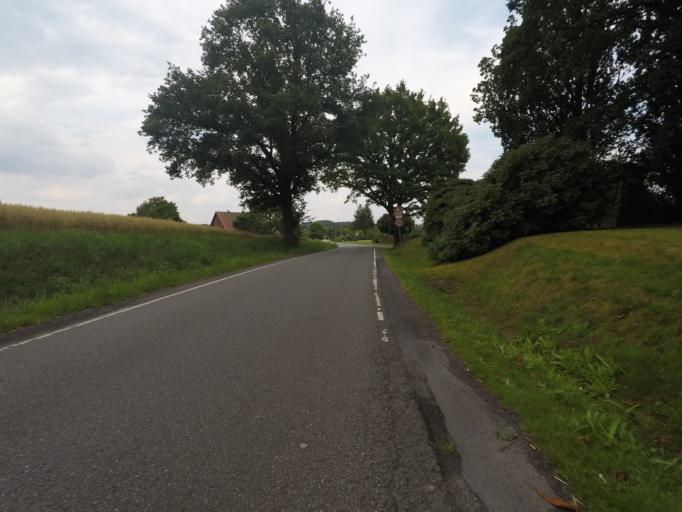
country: DE
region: North Rhine-Westphalia
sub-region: Regierungsbezirk Detmold
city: Herford
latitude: 52.1095
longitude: 8.6172
